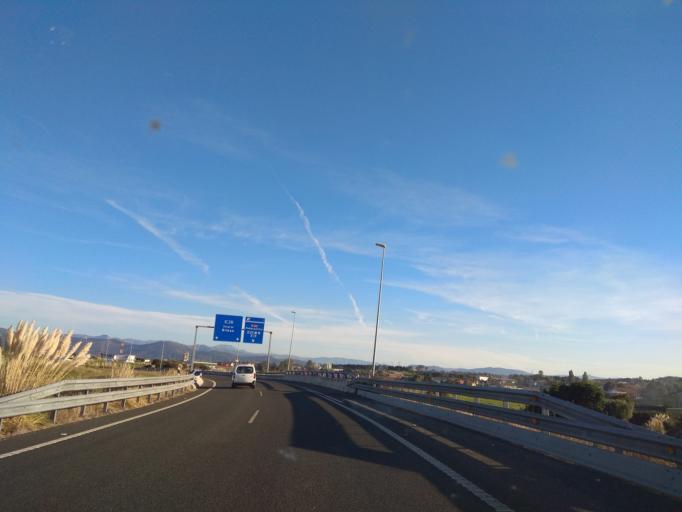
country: ES
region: Cantabria
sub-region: Provincia de Cantabria
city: Santa Cruz de Bezana
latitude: 43.4475
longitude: -3.8820
